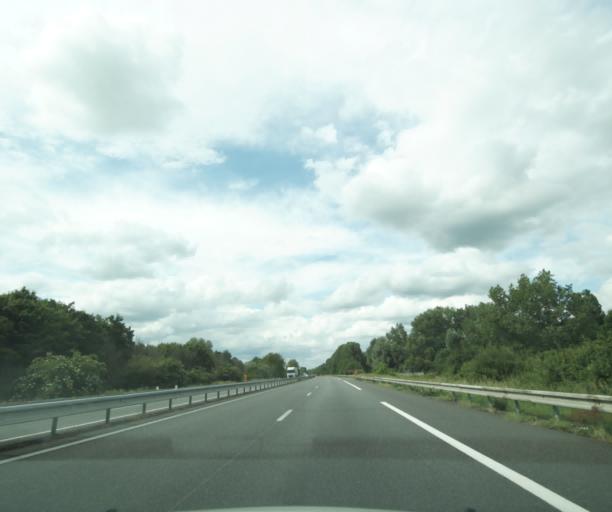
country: FR
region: Centre
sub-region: Departement du Cher
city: Foecy
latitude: 47.1673
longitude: 2.1815
